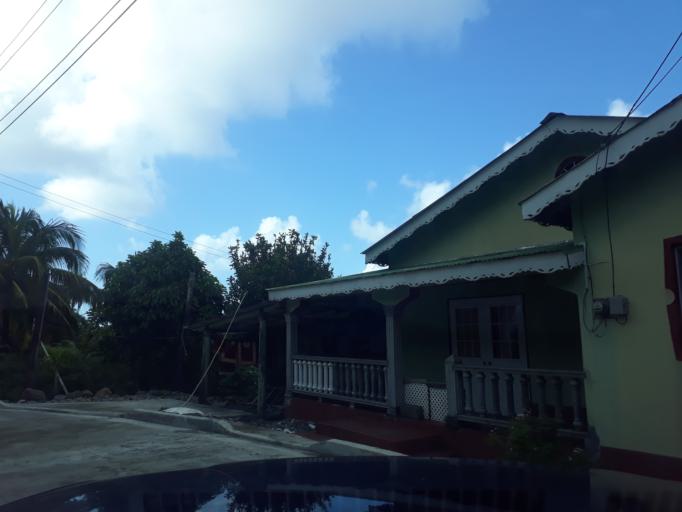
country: VC
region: Charlotte
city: Georgetown
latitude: 13.3805
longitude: -61.1714
